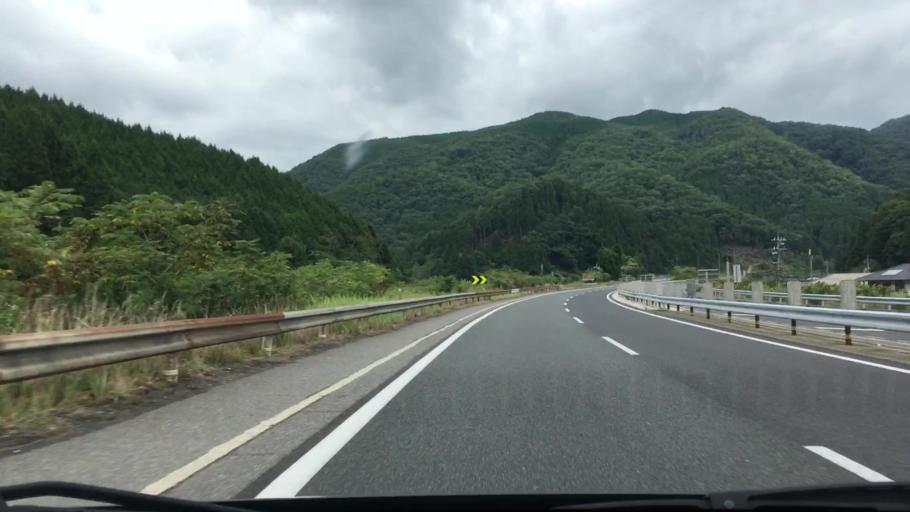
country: JP
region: Okayama
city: Niimi
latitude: 35.0057
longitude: 133.4852
